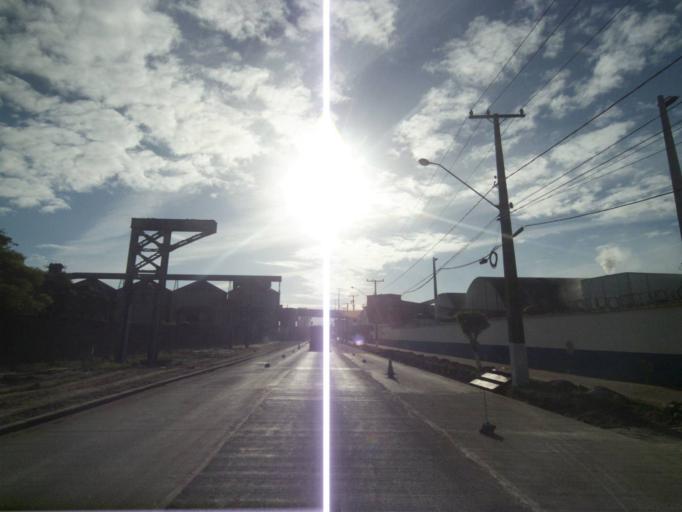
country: BR
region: Parana
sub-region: Paranagua
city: Paranagua
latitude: -25.5065
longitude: -48.5265
